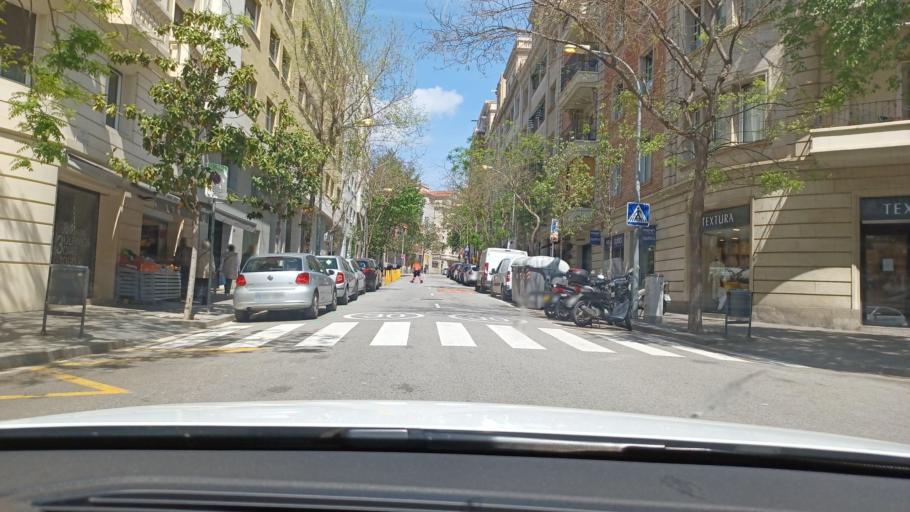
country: ES
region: Catalonia
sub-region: Provincia de Barcelona
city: les Corts
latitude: 41.3940
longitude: 2.1261
